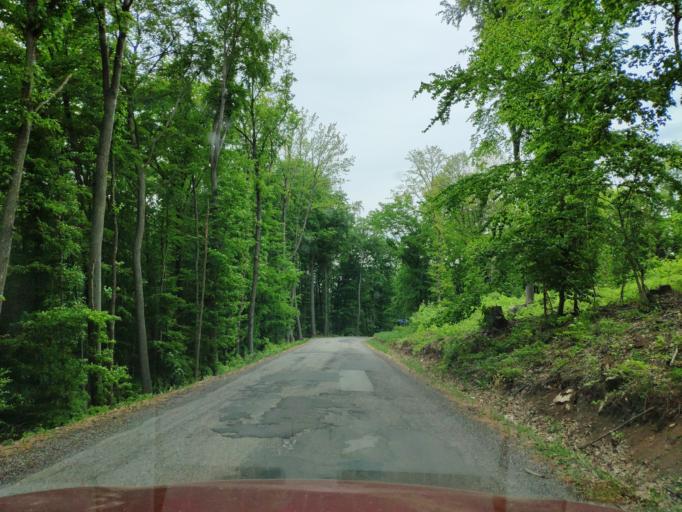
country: SK
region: Banskobystricky
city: Revuca
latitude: 48.5271
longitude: 20.1114
